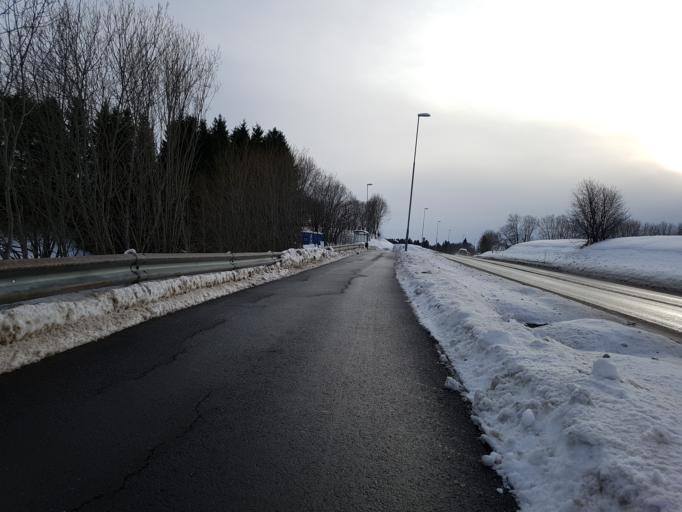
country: NO
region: Sor-Trondelag
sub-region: Trondheim
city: Trondheim
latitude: 63.3764
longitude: 10.3793
